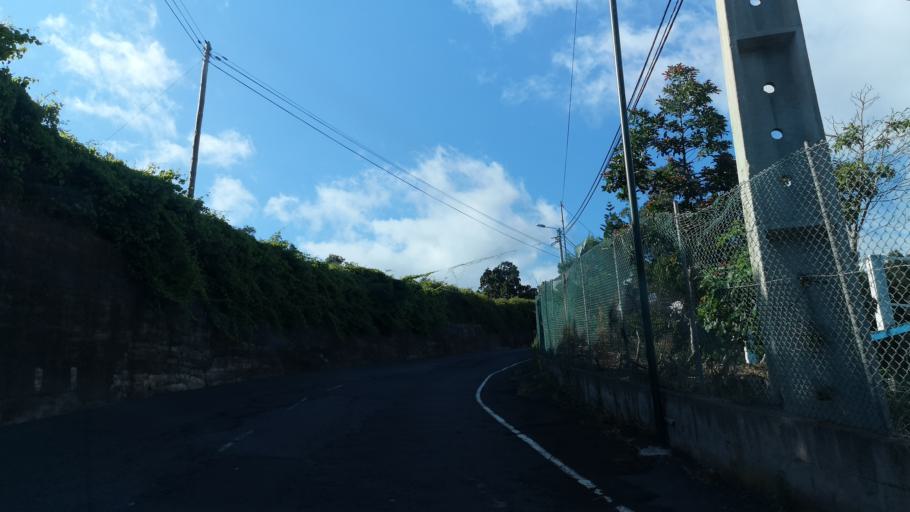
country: PT
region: Madeira
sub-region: Santa Cruz
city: Camacha
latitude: 32.6606
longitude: -16.8361
